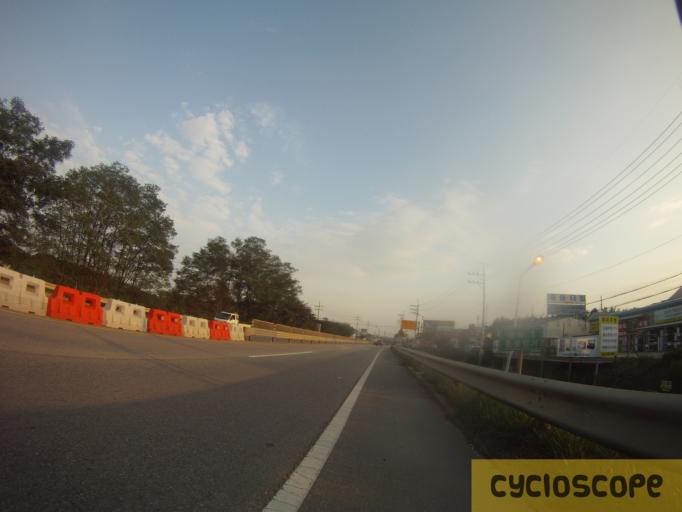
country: KR
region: Gyeonggi-do
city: Hwaseong-si
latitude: 37.1811
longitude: 126.9374
